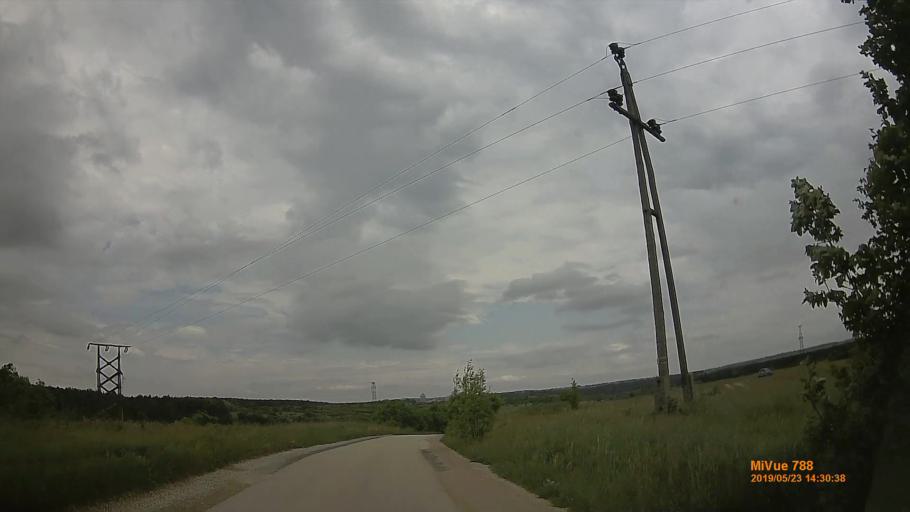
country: HU
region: Veszprem
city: Nemesvamos
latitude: 47.1057
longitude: 17.8581
